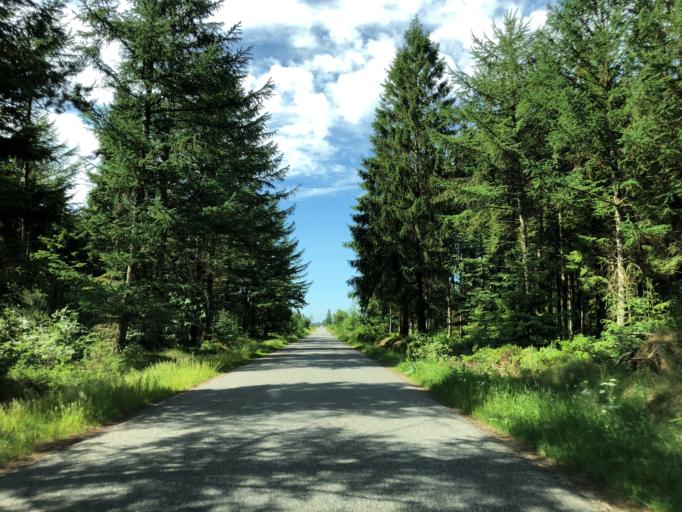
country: DK
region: Central Jutland
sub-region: Herning Kommune
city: Lind
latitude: 56.0453
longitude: 8.9317
